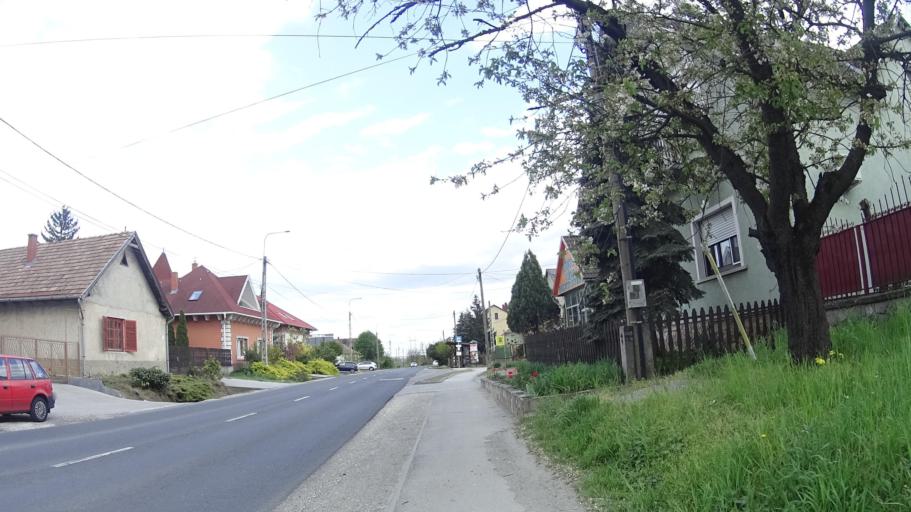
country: HU
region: Pest
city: Szada
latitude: 47.6291
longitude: 19.3206
